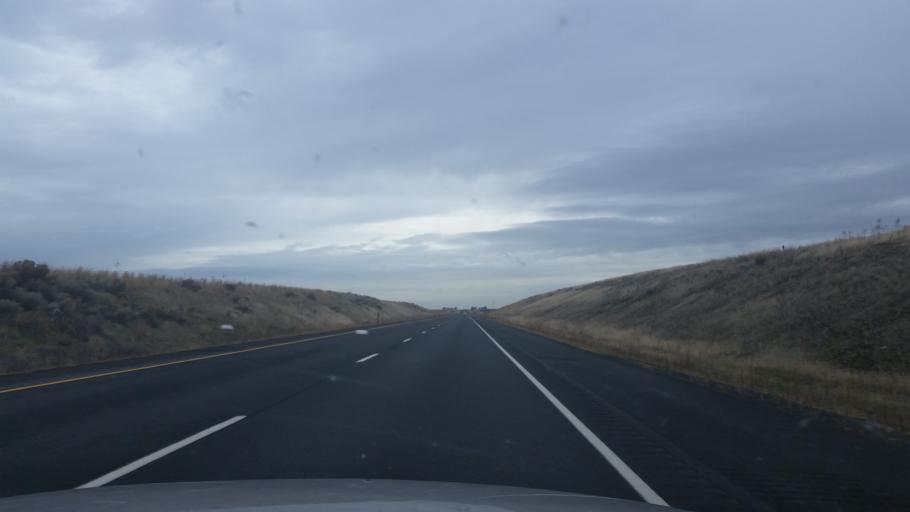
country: US
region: Washington
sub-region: Grant County
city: Warden
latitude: 47.0864
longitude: -118.7824
